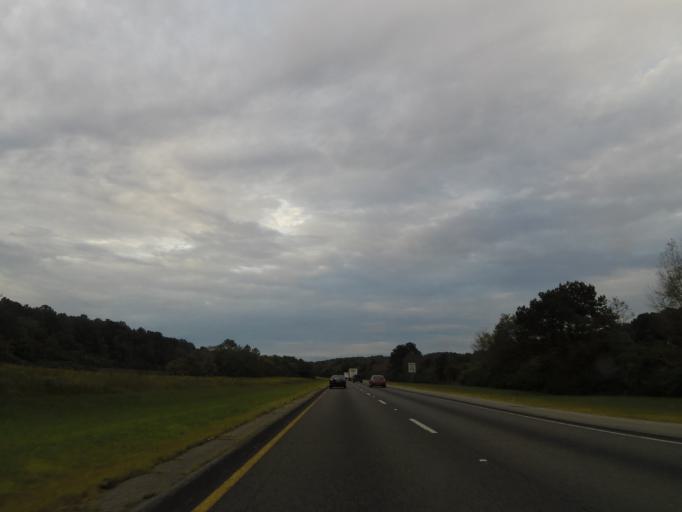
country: US
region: Alabama
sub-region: Jefferson County
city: Argo
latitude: 33.6656
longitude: -86.5586
